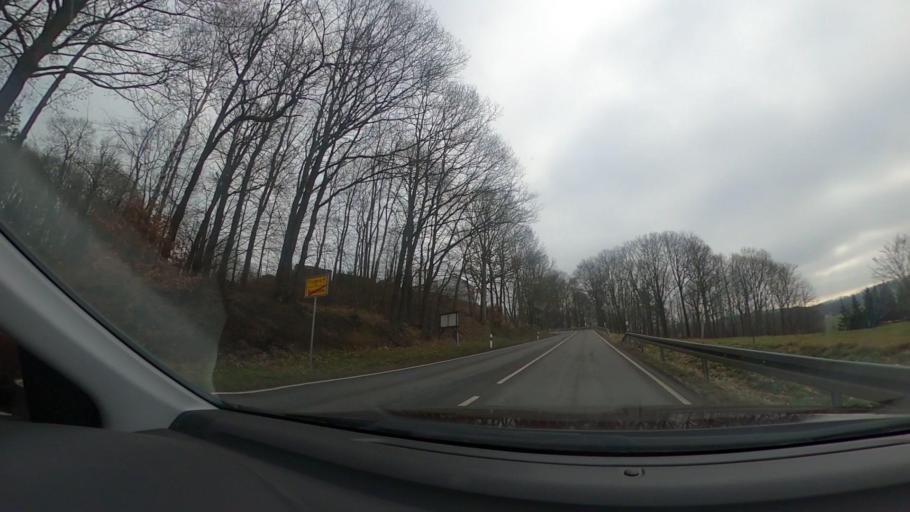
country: DE
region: Saxony
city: Oberschona
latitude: 50.9004
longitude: 13.2516
